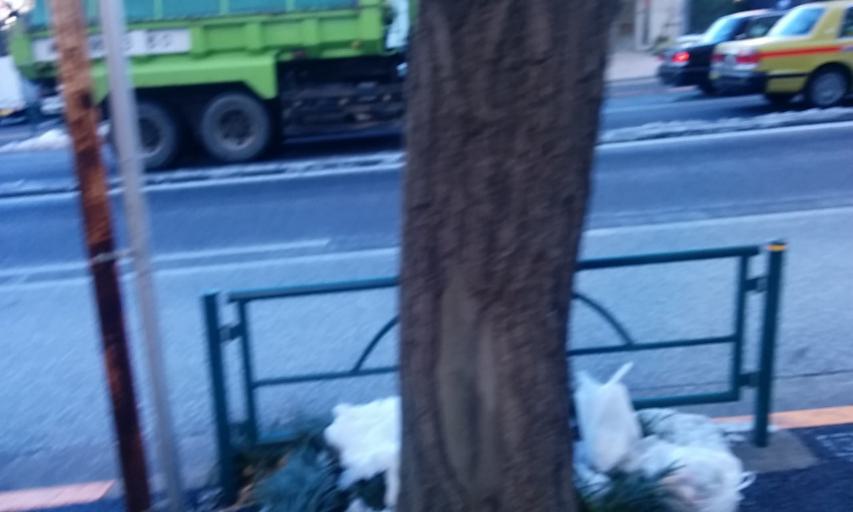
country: JP
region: Tokyo
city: Tokyo
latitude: 35.7208
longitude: 139.7558
